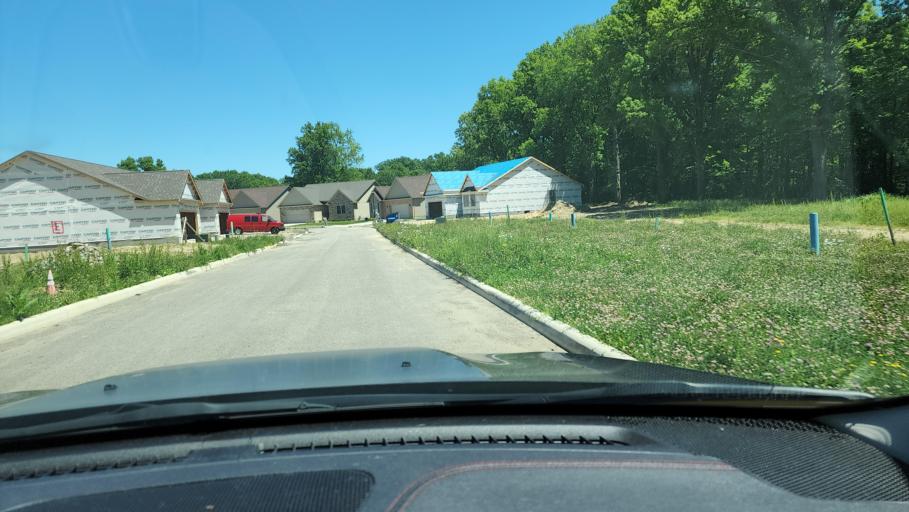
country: US
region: Ohio
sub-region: Trumbull County
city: McKinley Heights
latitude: 41.1920
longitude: -80.7404
